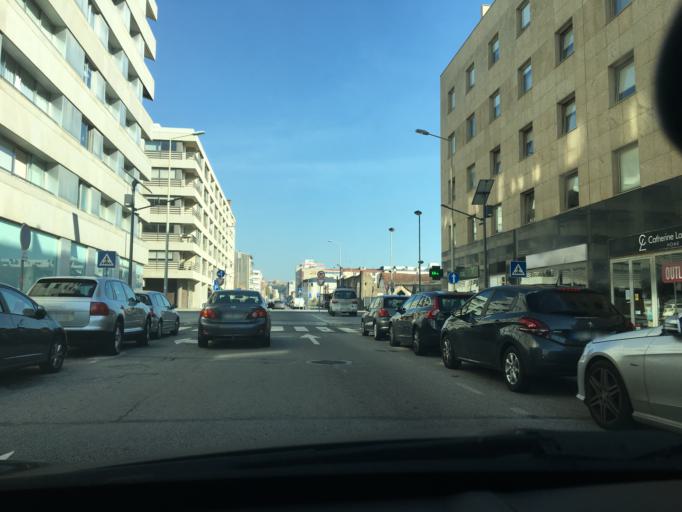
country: PT
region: Porto
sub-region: Matosinhos
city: Matosinhos
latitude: 41.1766
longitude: -8.6898
